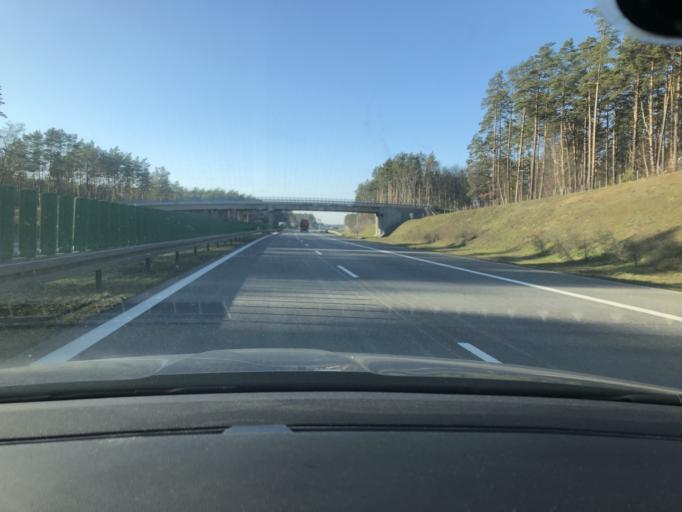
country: PL
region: Lubusz
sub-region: Powiat sulecinski
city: Torzym
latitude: 52.3253
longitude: 15.0587
